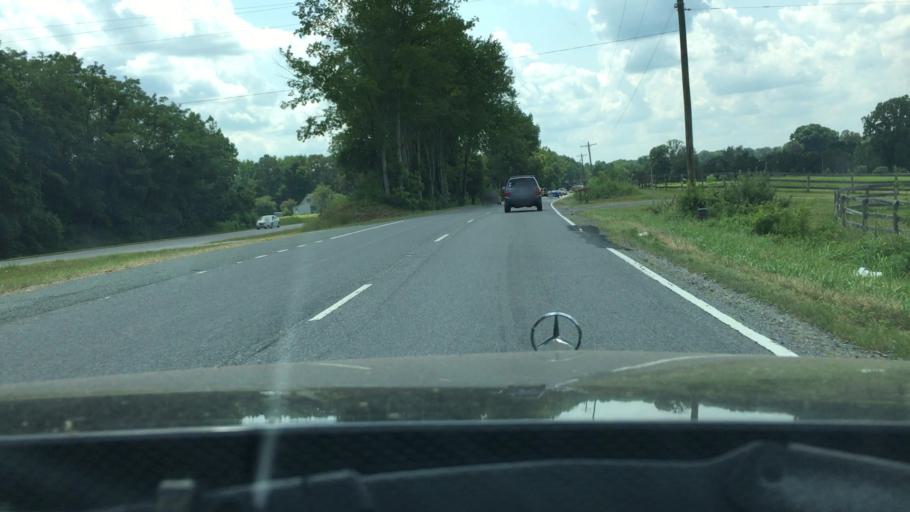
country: US
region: Virginia
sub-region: Spotsylvania County
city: Spotsylvania
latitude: 38.3103
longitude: -77.6665
